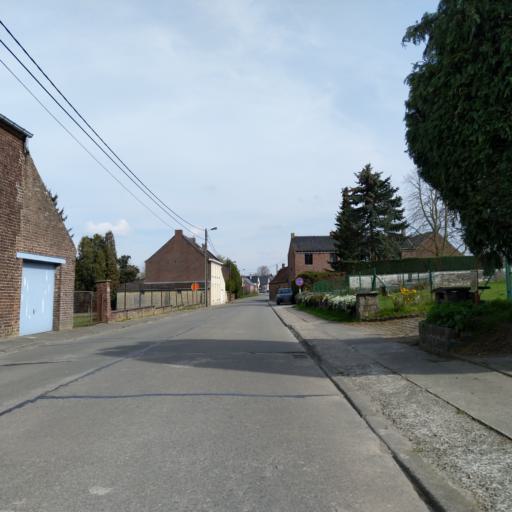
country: BE
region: Wallonia
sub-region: Province du Hainaut
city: Jurbise
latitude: 50.5353
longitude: 3.9637
